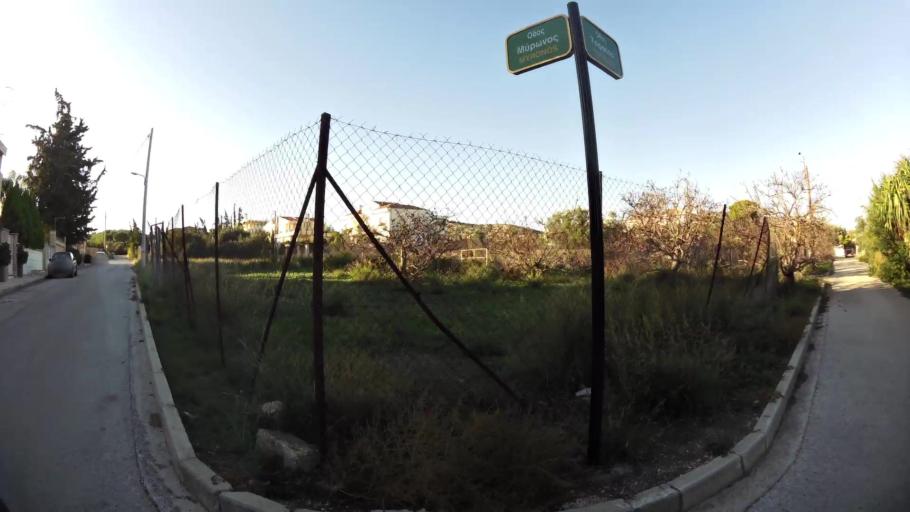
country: GR
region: Attica
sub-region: Nomarchia Anatolikis Attikis
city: Vari
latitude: 37.8230
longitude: 23.8024
